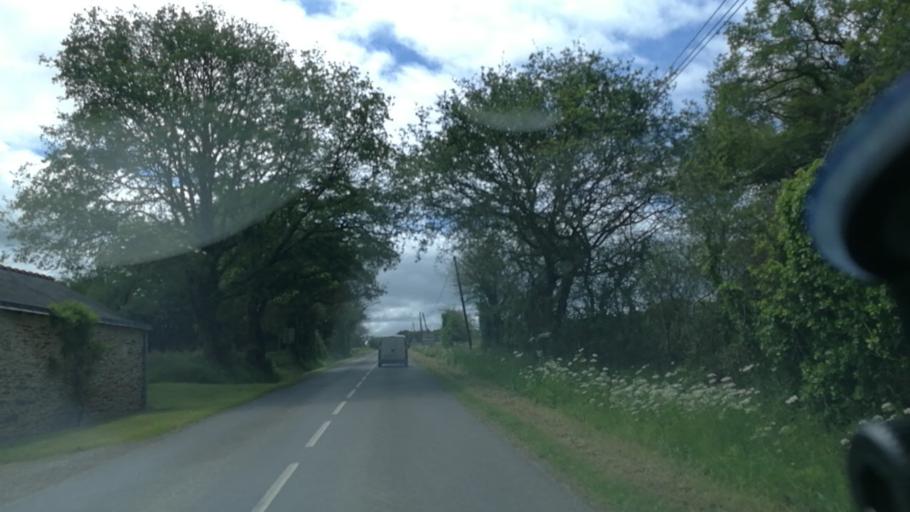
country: FR
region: Pays de la Loire
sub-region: Departement de la Loire-Atlantique
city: Asserac
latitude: 47.4592
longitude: -2.4230
